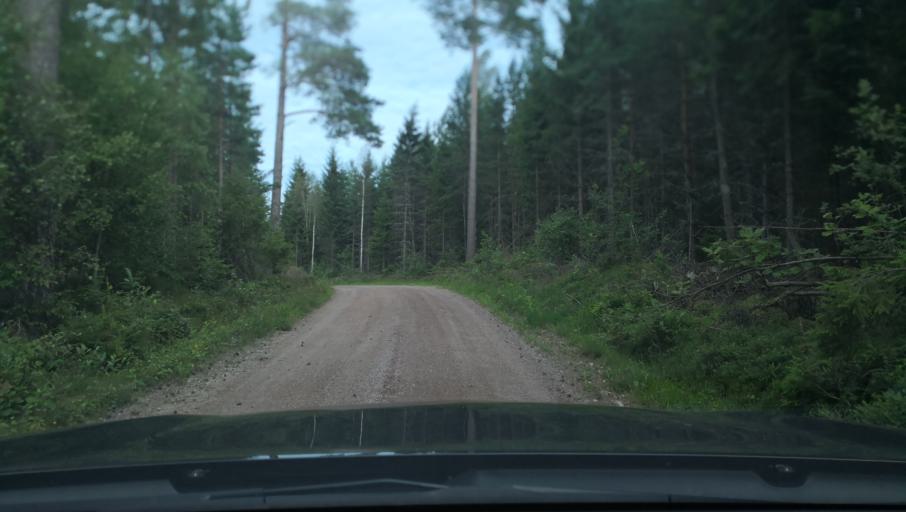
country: SE
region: Vaestmanland
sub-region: Surahammars Kommun
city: Surahammar
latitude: 59.6583
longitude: 16.1319
